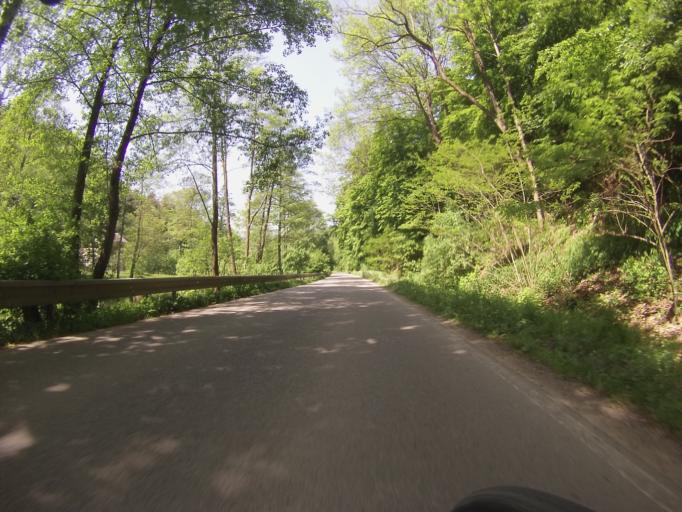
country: CZ
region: South Moravian
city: Bilovice nad Svitavou
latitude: 49.2551
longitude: 16.6709
